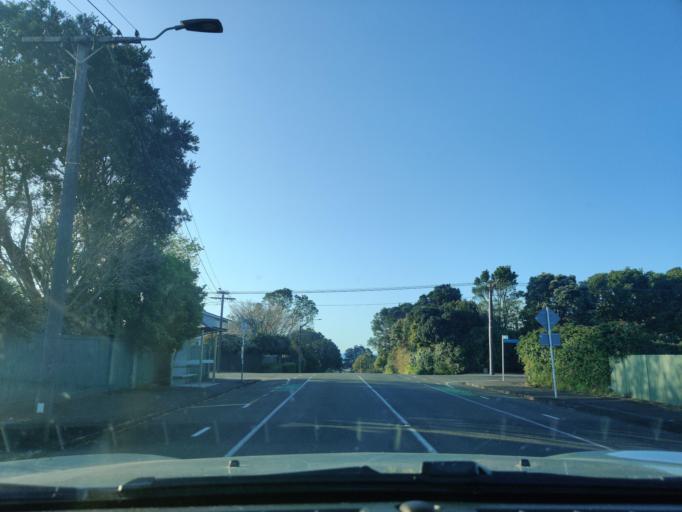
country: NZ
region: Taranaki
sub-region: New Plymouth District
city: New Plymouth
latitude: -39.0665
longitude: 174.0658
